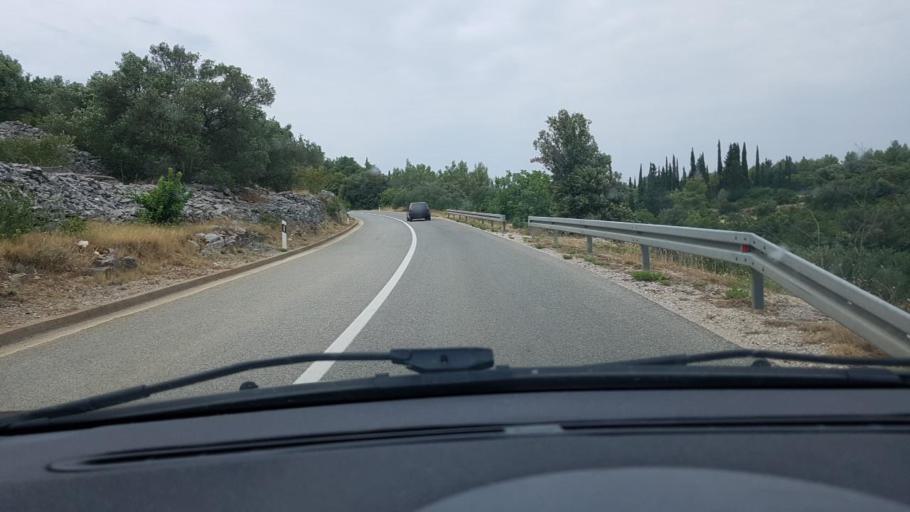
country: HR
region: Dubrovacko-Neretvanska
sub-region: Grad Korcula
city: Zrnovo
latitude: 42.9376
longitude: 17.0971
